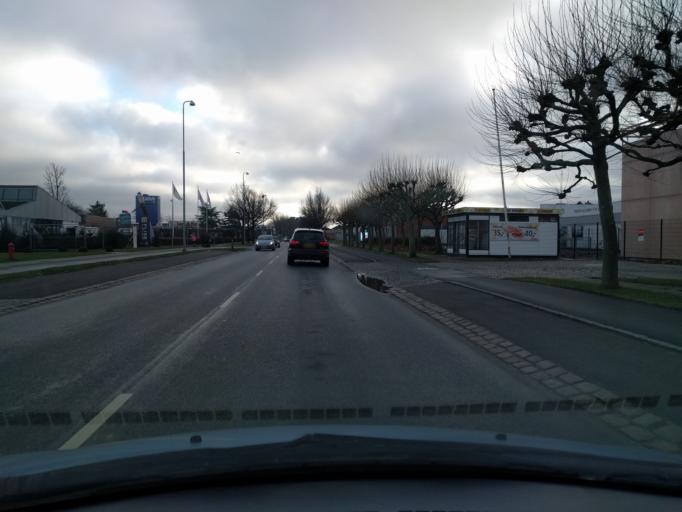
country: DK
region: South Denmark
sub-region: Odense Kommune
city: Neder Holluf
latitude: 55.3820
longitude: 10.4198
